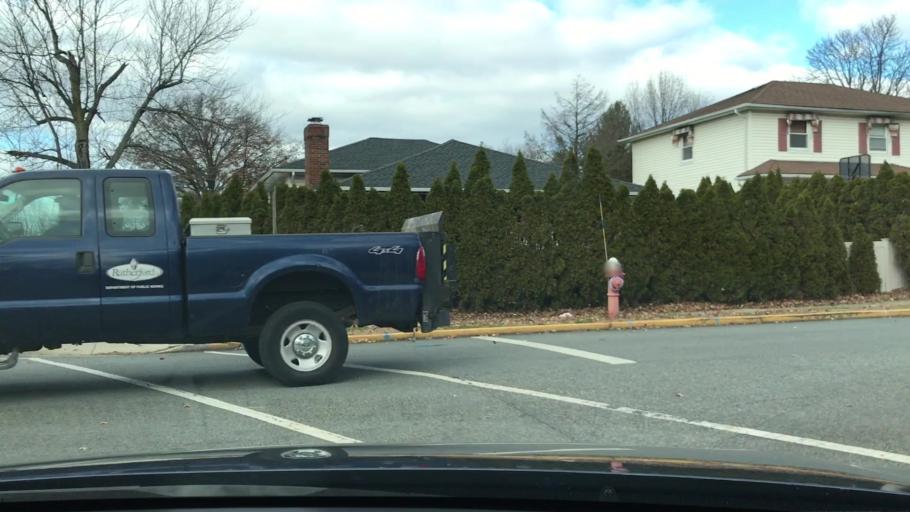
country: US
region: New Jersey
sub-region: Bergen County
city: Rutherford
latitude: 40.8301
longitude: -74.1137
